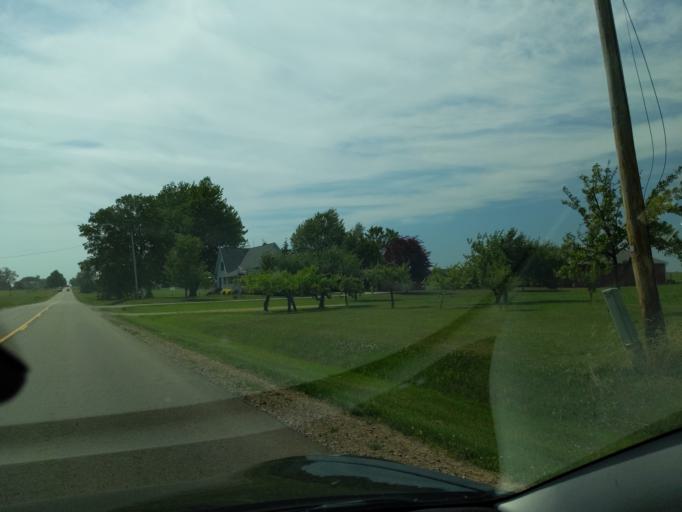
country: US
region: Michigan
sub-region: Eaton County
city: Grand Ledge
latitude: 42.7120
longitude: -84.8425
